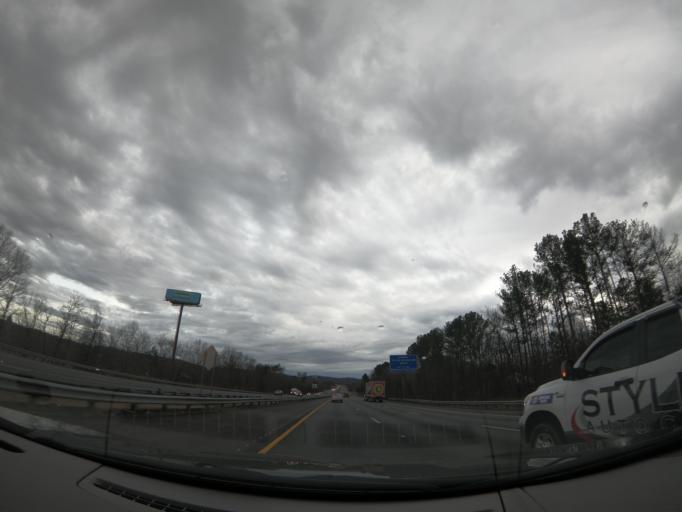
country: US
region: Georgia
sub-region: Catoosa County
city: Indian Springs
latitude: 34.9615
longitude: -85.1838
